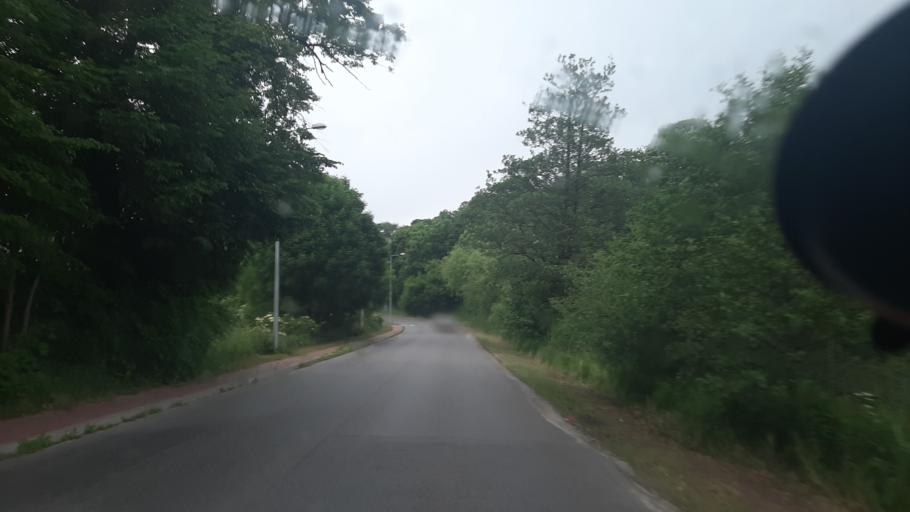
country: PL
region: Lublin Voivodeship
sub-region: Powiat lubelski
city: Garbow
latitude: 51.3527
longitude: 22.3309
